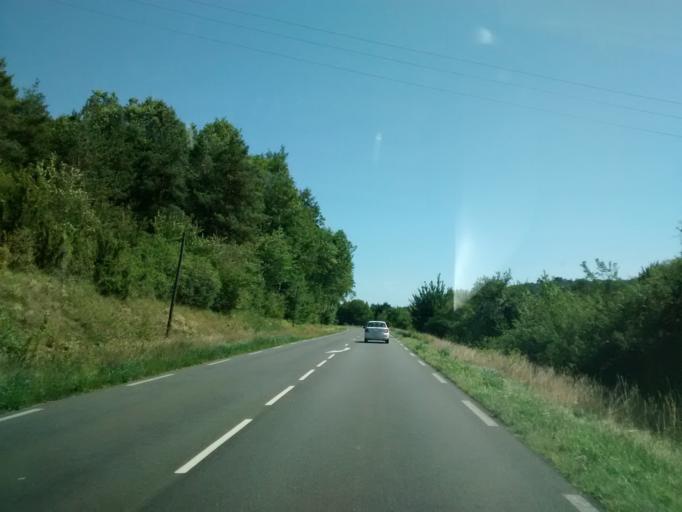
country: FR
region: Aquitaine
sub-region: Departement de la Dordogne
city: Bassillac
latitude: 45.1308
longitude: 0.8159
